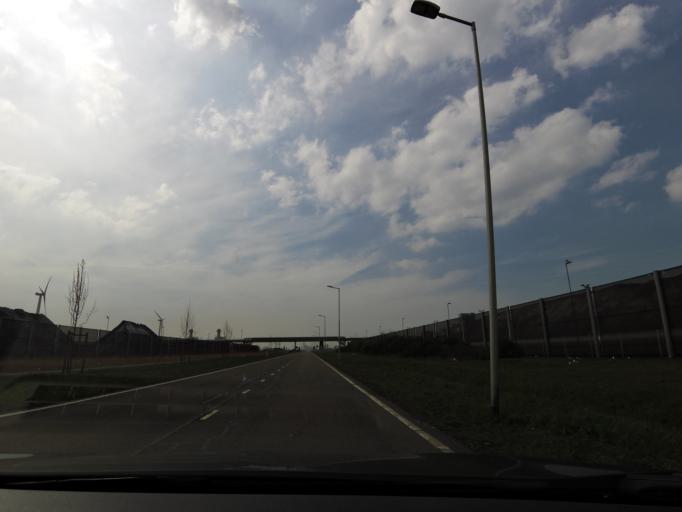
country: NL
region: South Holland
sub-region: Gemeente Rotterdam
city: Hoek van Holland
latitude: 51.9556
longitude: 4.1056
